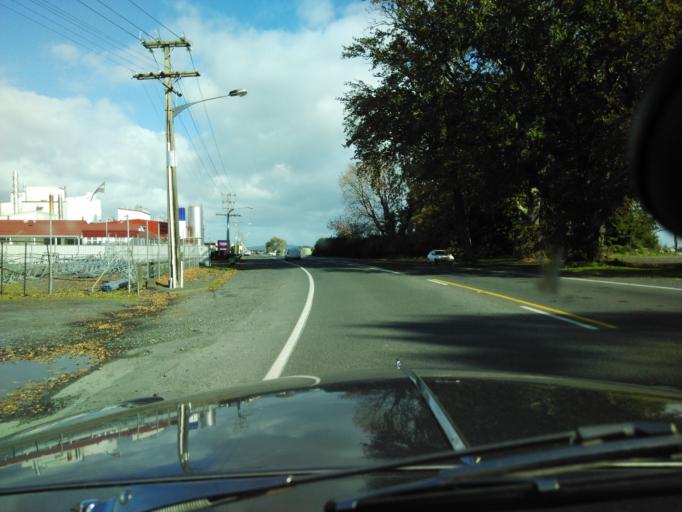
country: NZ
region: Waikato
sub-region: Matamata-Piako District
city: Matamata
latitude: -37.6227
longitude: 175.5934
